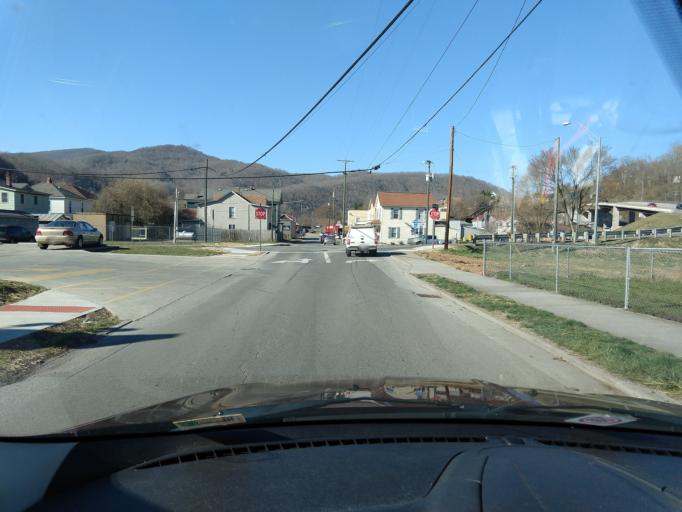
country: US
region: West Virginia
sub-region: Summers County
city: Hinton
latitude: 37.6669
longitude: -80.8922
